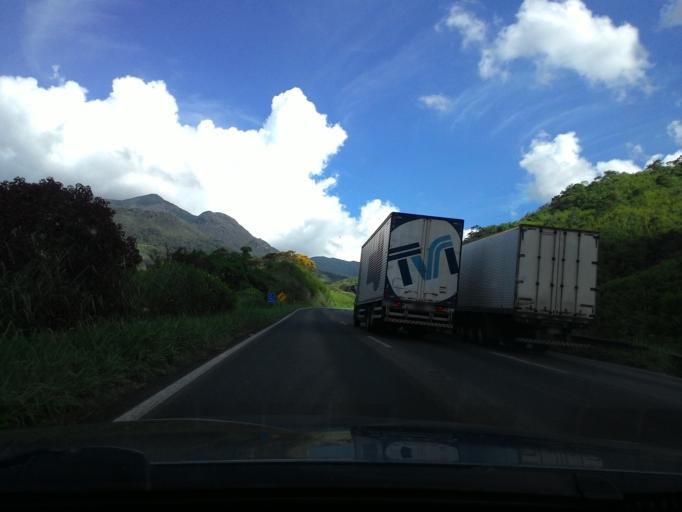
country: BR
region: Sao Paulo
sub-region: Cajati
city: Cajati
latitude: -24.8436
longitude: -48.2201
